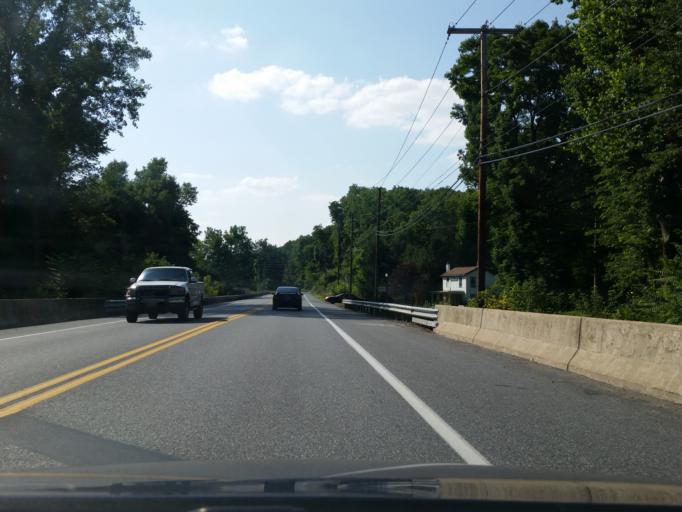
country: US
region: Pennsylvania
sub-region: Lancaster County
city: Marietta
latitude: 40.0553
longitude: -76.5254
